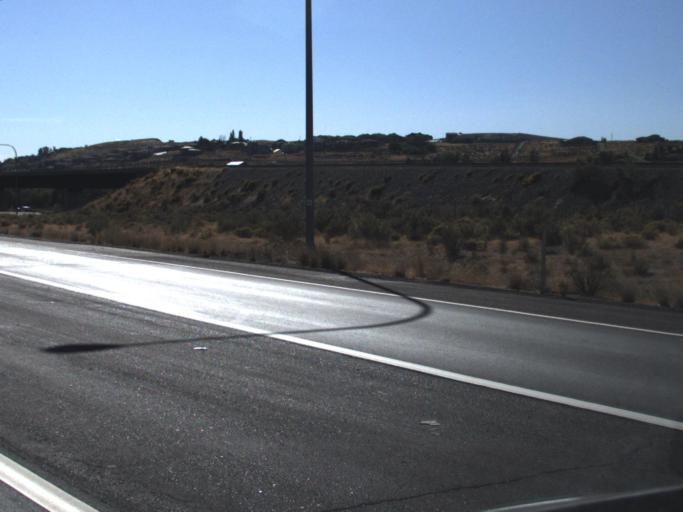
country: US
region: Washington
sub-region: Benton County
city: Richland
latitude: 46.2608
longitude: -119.2900
